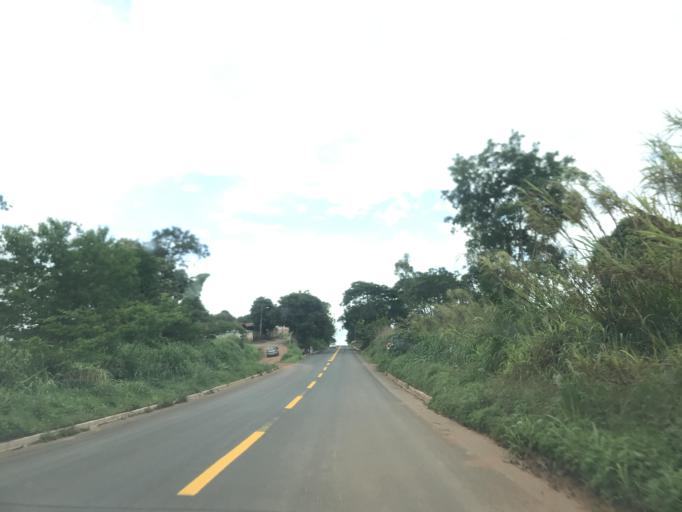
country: BR
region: Goias
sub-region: Bela Vista De Goias
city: Bela Vista de Goias
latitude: -17.0648
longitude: -48.6576
